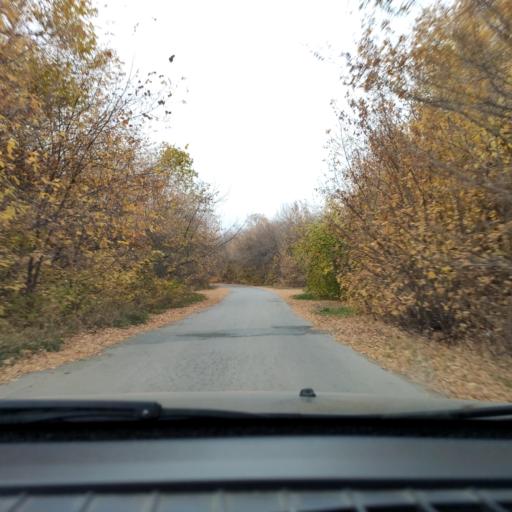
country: RU
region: Samara
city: Tol'yatti
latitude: 53.4966
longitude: 49.2648
